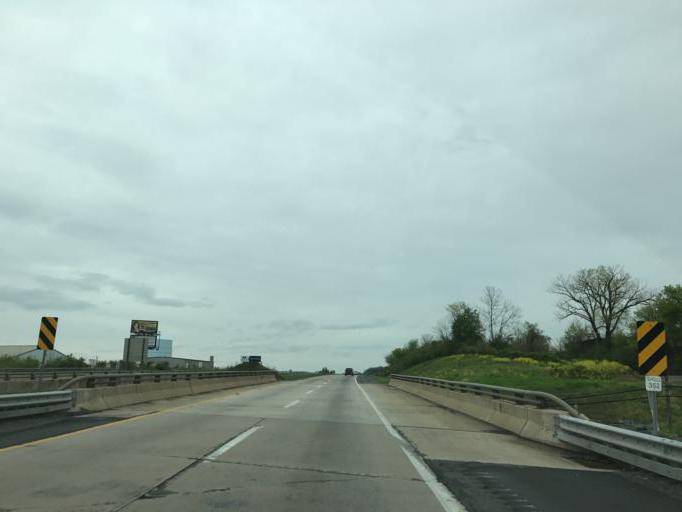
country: US
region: Pennsylvania
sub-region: Berks County
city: Temple
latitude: 40.4183
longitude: -75.9274
